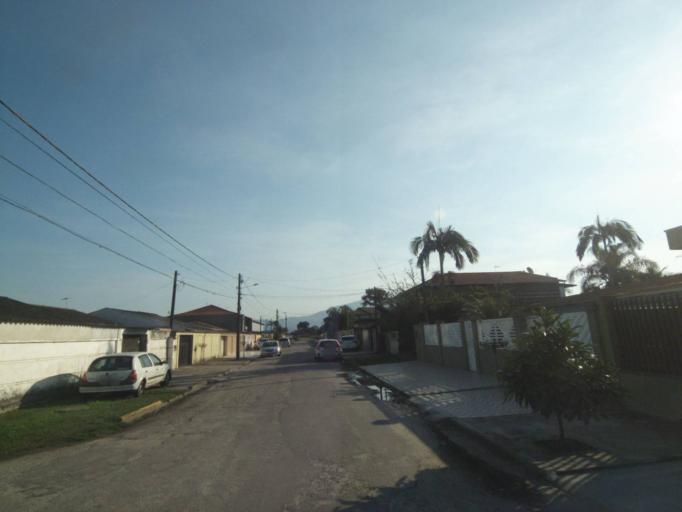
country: BR
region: Parana
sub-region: Paranagua
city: Paranagua
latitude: -25.5587
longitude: -48.5621
